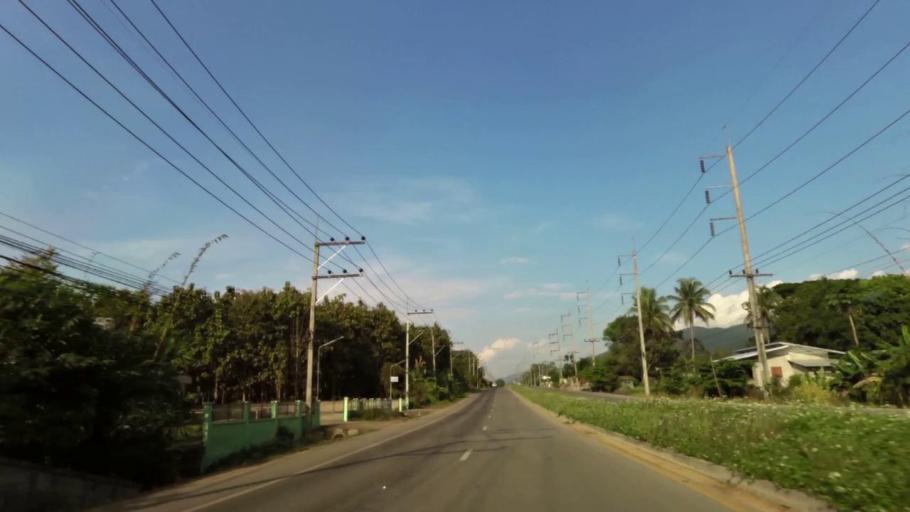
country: TH
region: Chiang Rai
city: Khun Tan
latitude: 19.8733
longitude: 100.2869
